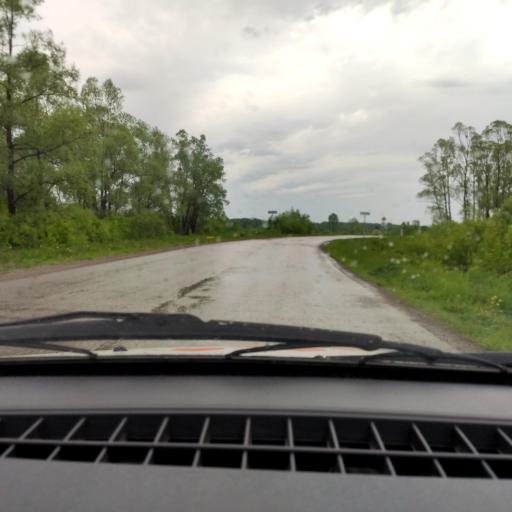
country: RU
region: Bashkortostan
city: Urman
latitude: 54.8638
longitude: 56.8406
